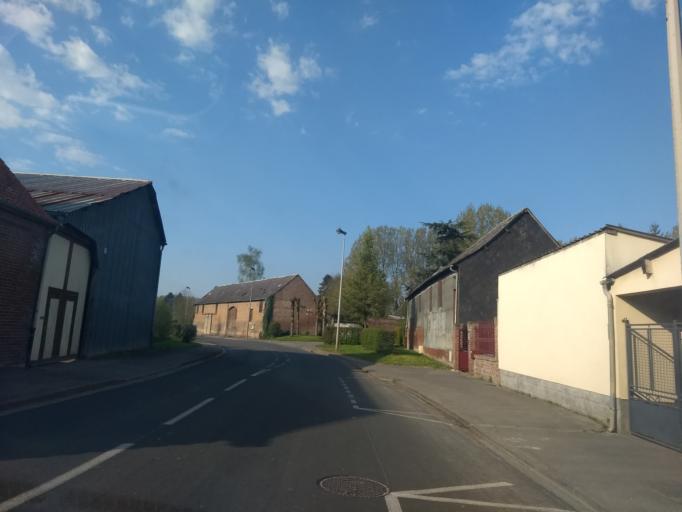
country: FR
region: Picardie
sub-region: Departement de la Somme
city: Corbie
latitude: 50.0035
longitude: 2.4734
